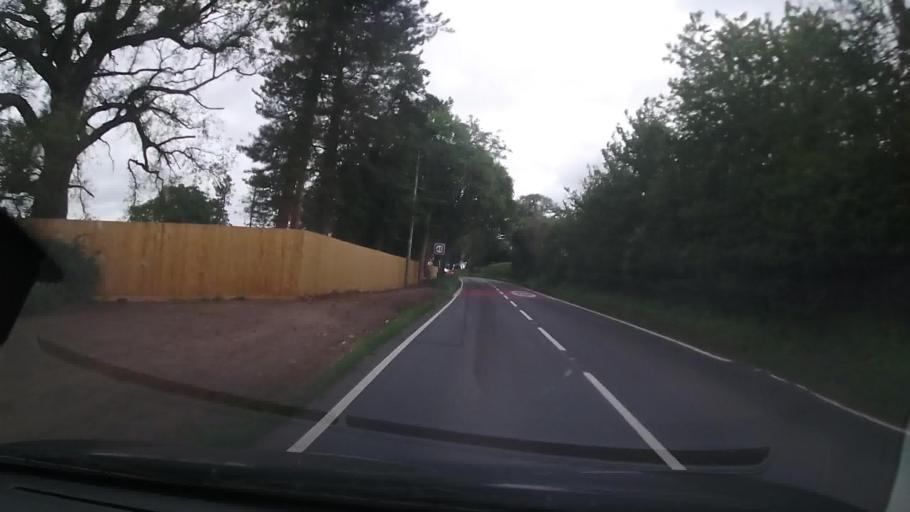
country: GB
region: England
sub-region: Shropshire
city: Astley
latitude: 52.7614
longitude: -2.7472
